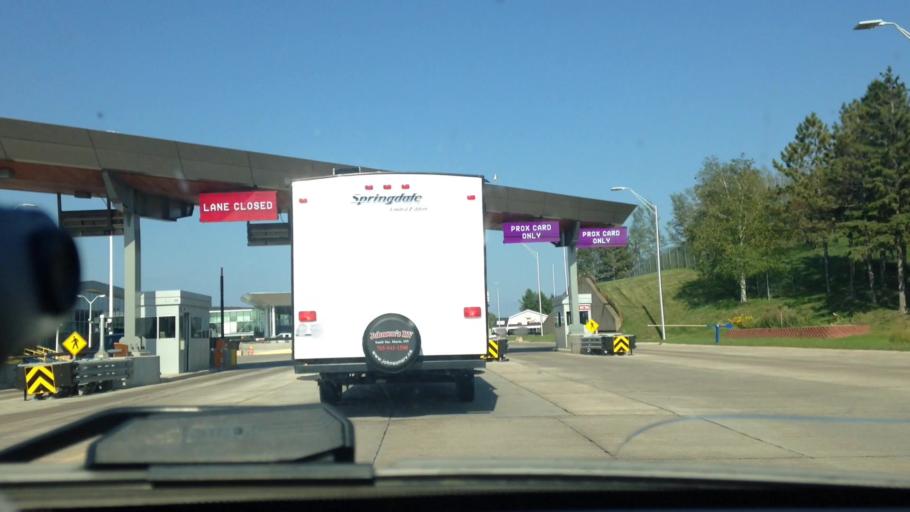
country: US
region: Michigan
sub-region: Chippewa County
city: Sault Ste. Marie
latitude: 46.4933
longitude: -84.3690
